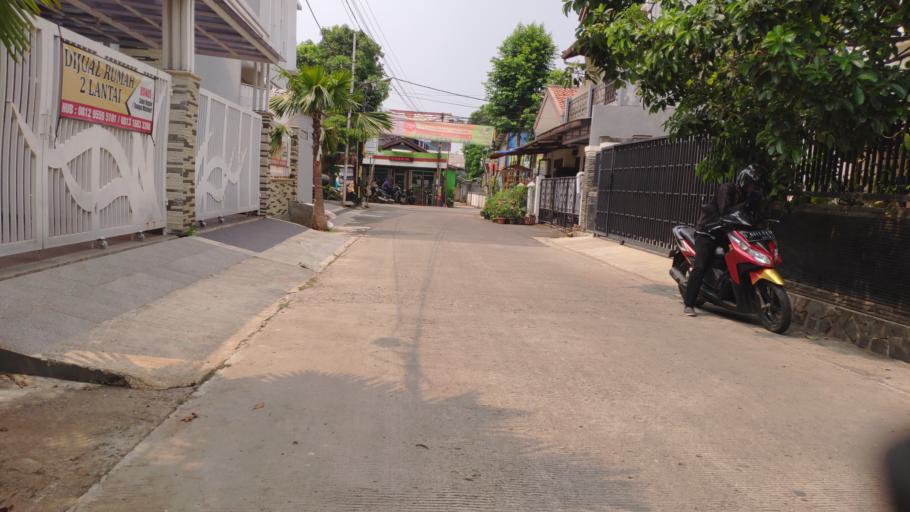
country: ID
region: West Java
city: Depok
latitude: -6.3685
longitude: 106.8053
